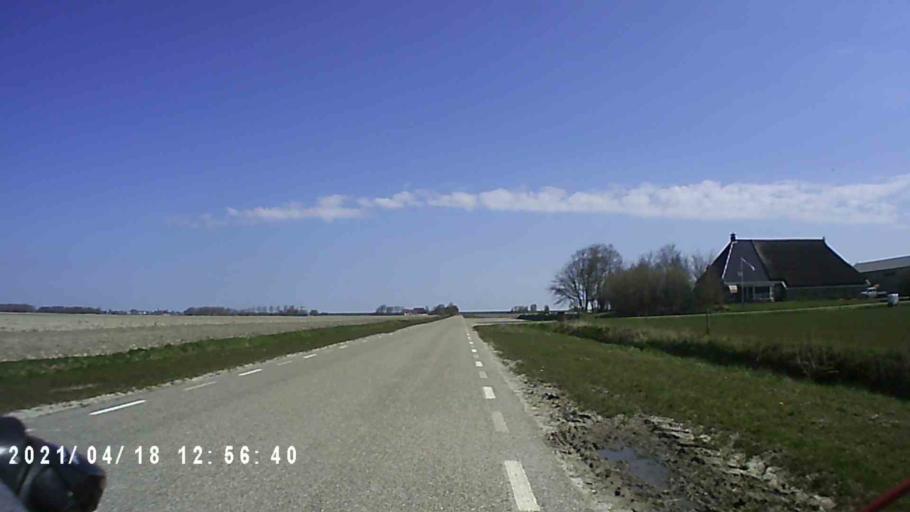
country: NL
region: Friesland
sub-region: Gemeente Dongeradeel
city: Anjum
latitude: 53.3947
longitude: 6.0894
